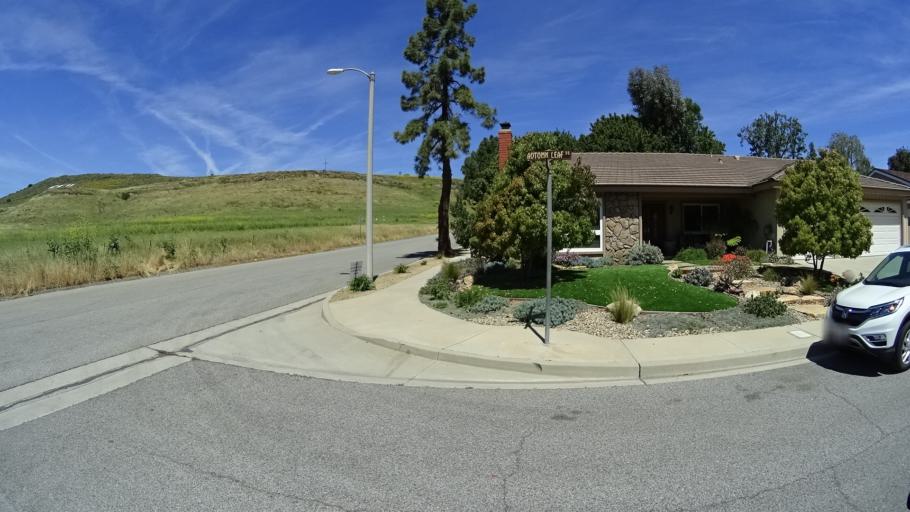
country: US
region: California
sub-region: Ventura County
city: Moorpark
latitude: 34.2317
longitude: -118.8756
